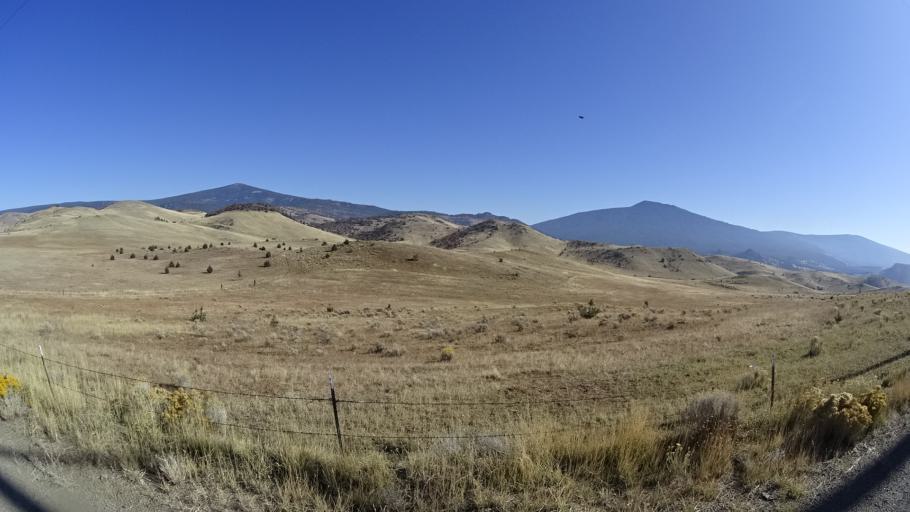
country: US
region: California
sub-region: Siskiyou County
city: Montague
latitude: 41.7708
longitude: -122.3591
